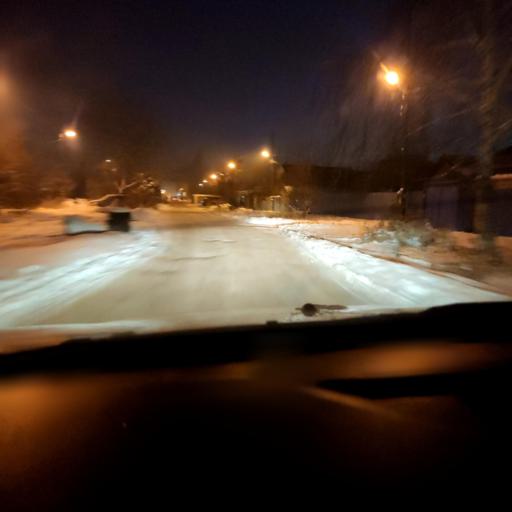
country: RU
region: Samara
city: Petra-Dubrava
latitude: 53.2469
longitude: 50.3217
